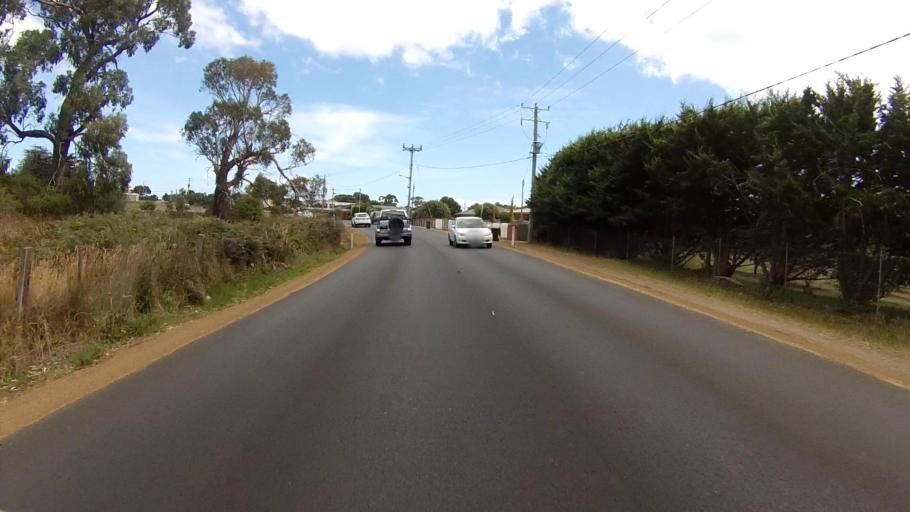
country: AU
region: Tasmania
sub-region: Sorell
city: Sorell
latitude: -42.8504
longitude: 147.6241
